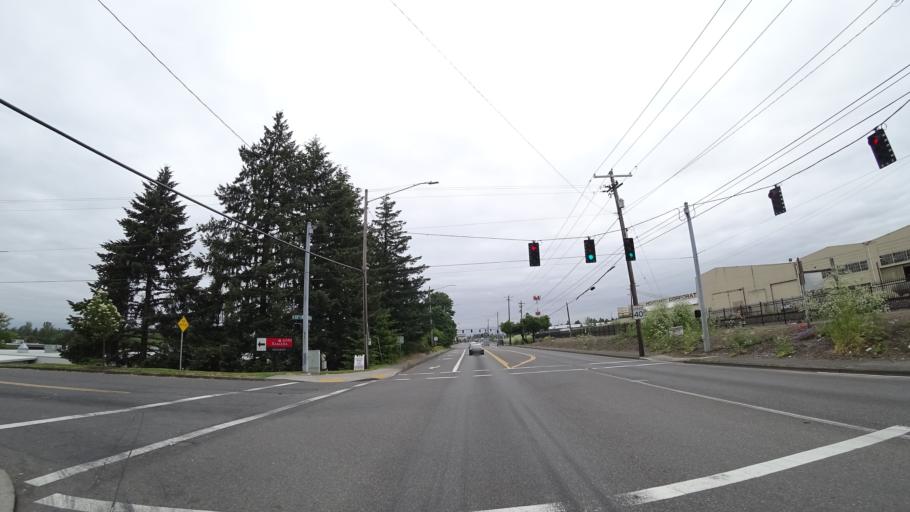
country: US
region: Oregon
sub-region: Multnomah County
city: Lents
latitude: 45.5652
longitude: -122.5806
